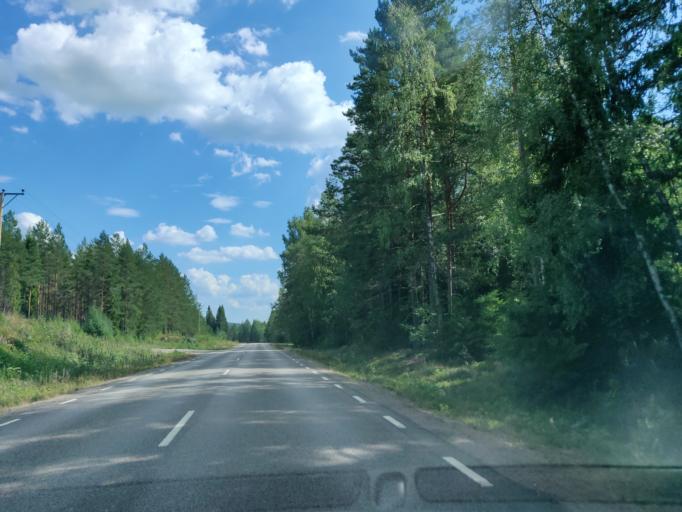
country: SE
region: Vaermland
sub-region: Munkfors Kommun
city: Munkfors
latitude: 59.8563
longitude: 13.6223
